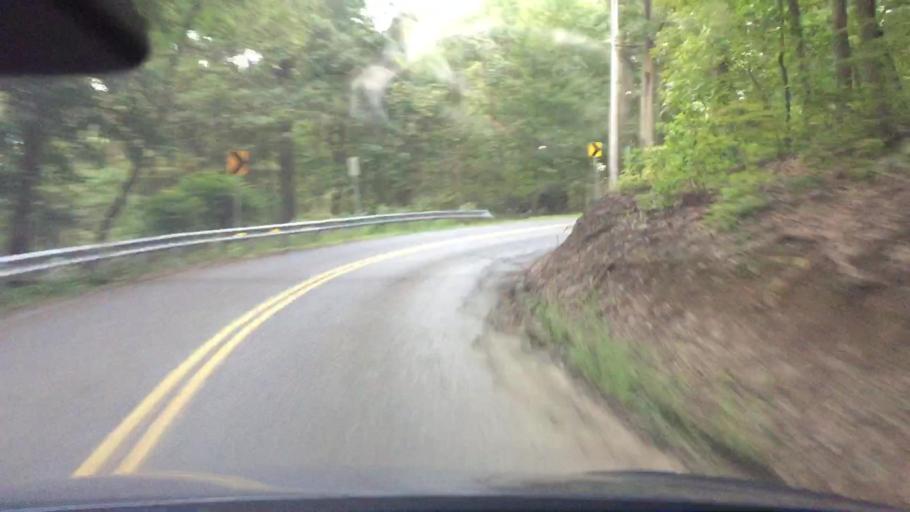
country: US
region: Pennsylvania
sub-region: Allegheny County
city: Bakerstown
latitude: 40.6423
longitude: -79.8977
